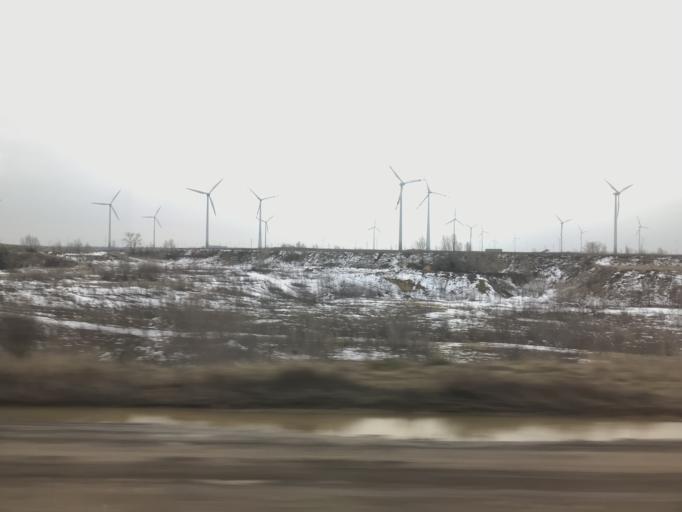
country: AT
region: Burgenland
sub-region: Politischer Bezirk Neusiedl am See
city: Parndorf
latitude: 47.9887
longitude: 16.9129
